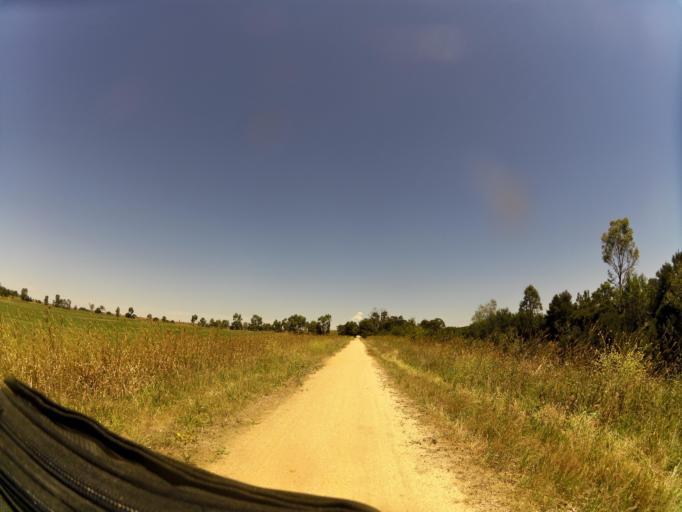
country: AU
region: Victoria
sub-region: Wellington
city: Sale
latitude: -37.9794
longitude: 147.0477
